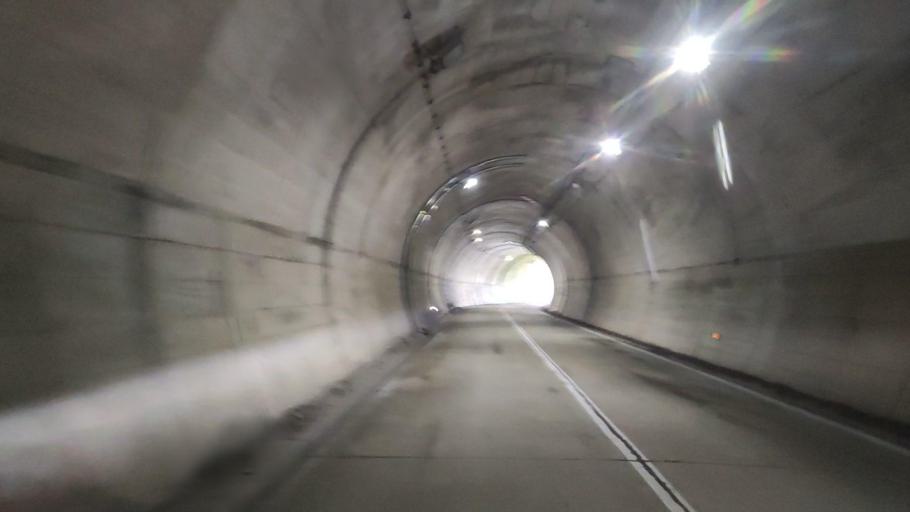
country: JP
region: Fukui
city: Ono
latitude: 35.9227
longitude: 136.5454
